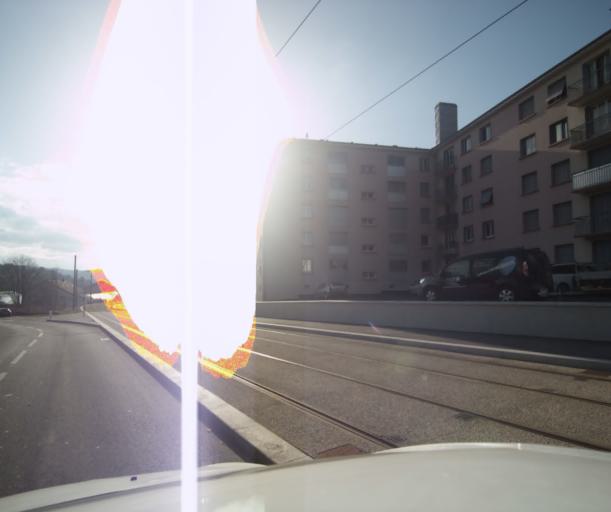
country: FR
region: Franche-Comte
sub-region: Departement du Doubs
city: Besancon
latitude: 47.2551
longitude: 6.0450
